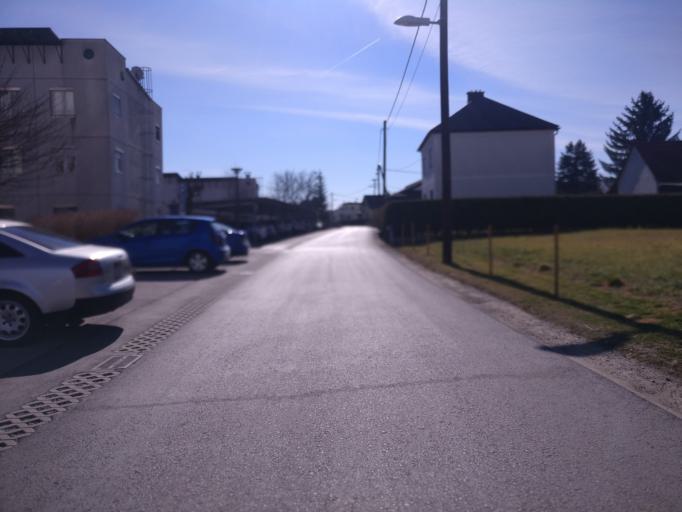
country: AT
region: Styria
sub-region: Politischer Bezirk Graz-Umgebung
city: Feldkirchen bei Graz
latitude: 47.0161
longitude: 15.4476
